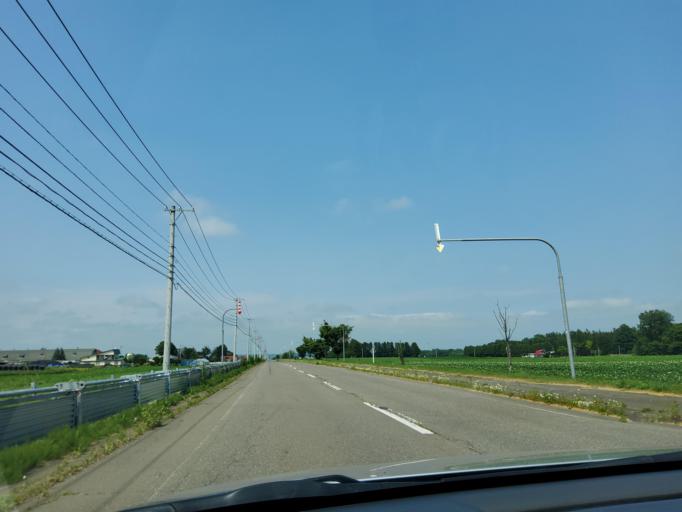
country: JP
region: Hokkaido
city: Obihiro
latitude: 42.8730
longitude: 143.0258
